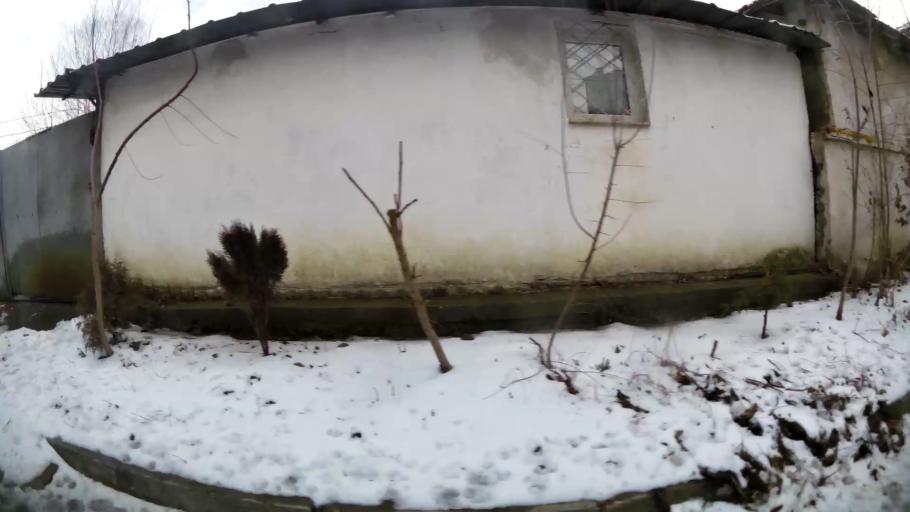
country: BG
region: Sofia-Capital
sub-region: Stolichna Obshtina
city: Sofia
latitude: 42.7226
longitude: 23.3325
